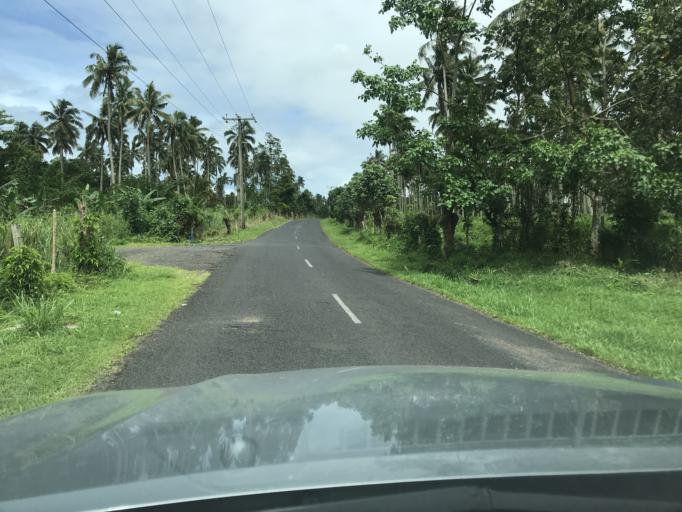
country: WS
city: Nofoali`i
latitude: -13.8732
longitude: -171.9224
